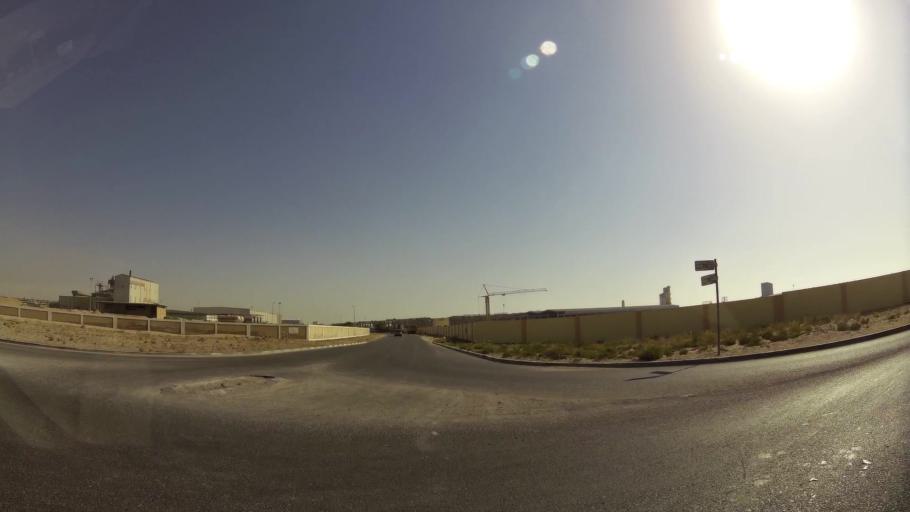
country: AE
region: Dubai
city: Dubai
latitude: 25.0001
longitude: 55.1215
